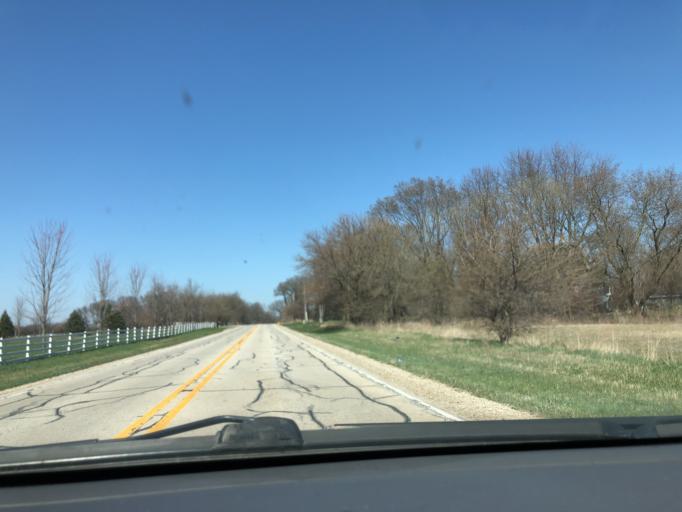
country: US
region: Illinois
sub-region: McHenry County
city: Huntley
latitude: 42.1632
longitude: -88.4787
